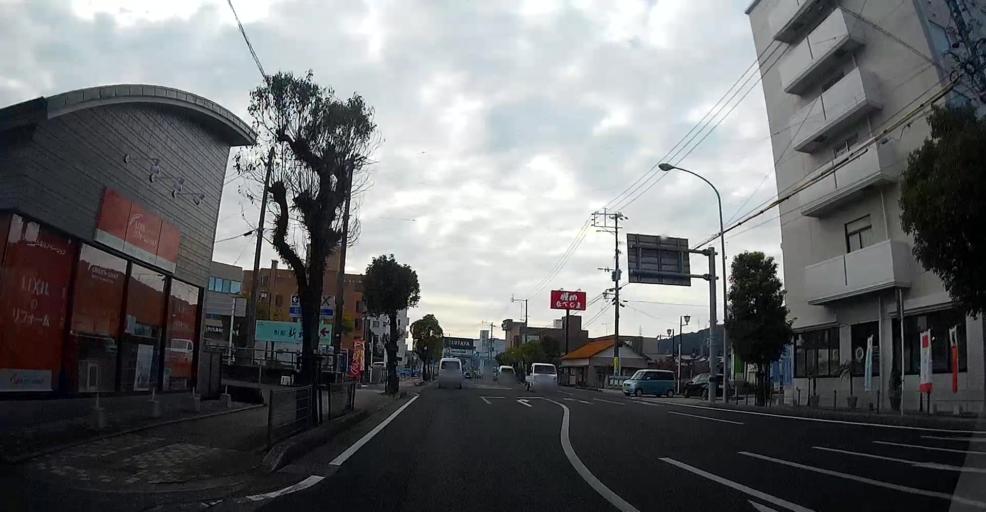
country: JP
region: Kumamoto
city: Hondo
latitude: 32.4553
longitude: 130.1940
